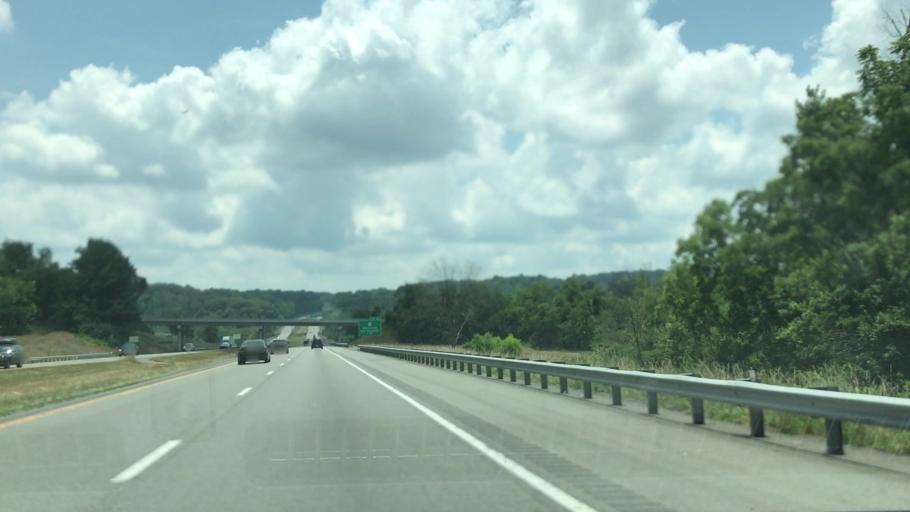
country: US
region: Virginia
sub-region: Wythe County
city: Wytheville
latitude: 36.9891
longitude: -81.0763
